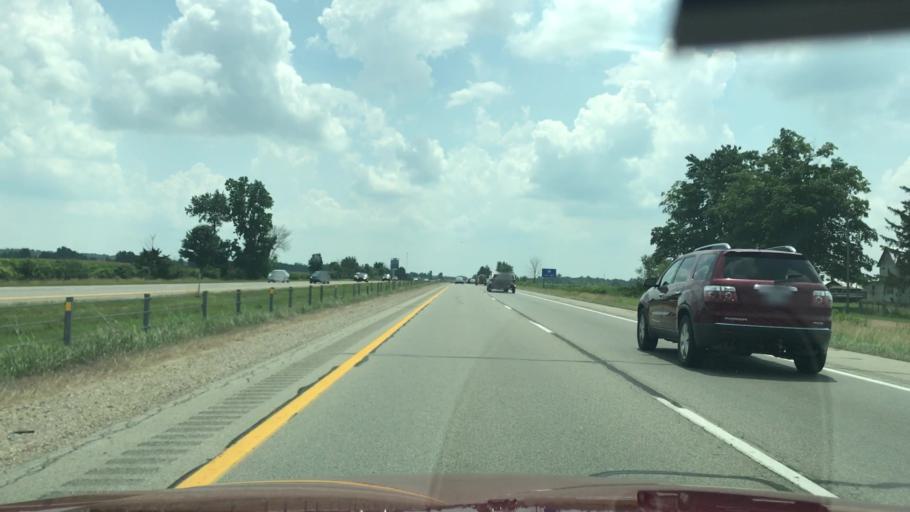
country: US
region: Michigan
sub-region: Allegan County
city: Wayland
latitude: 42.6437
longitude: -85.6623
